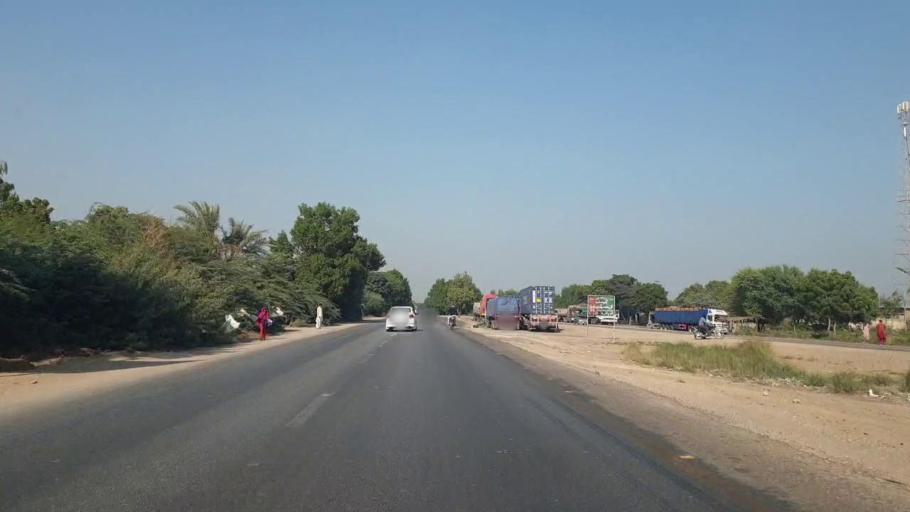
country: PK
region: Sindh
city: Matiari
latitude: 25.5032
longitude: 68.4258
